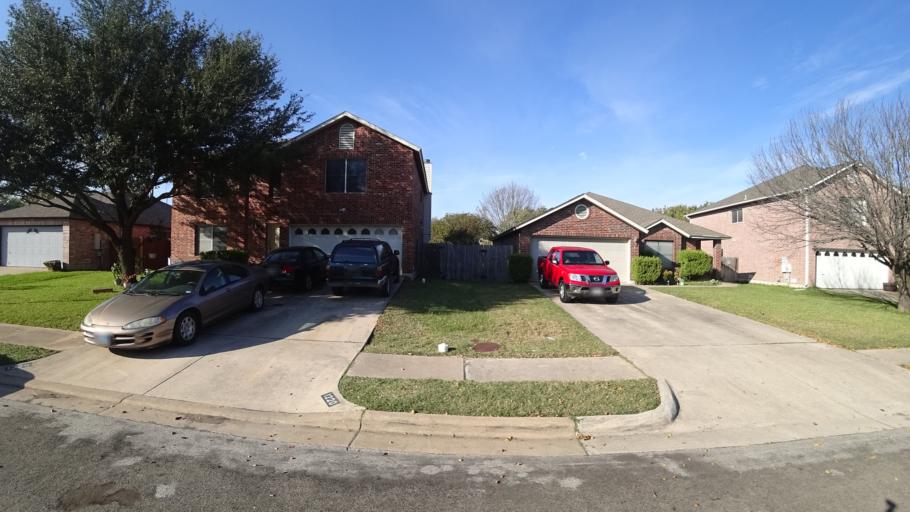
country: US
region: Texas
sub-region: Travis County
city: Pflugerville
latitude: 30.4001
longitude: -97.6502
